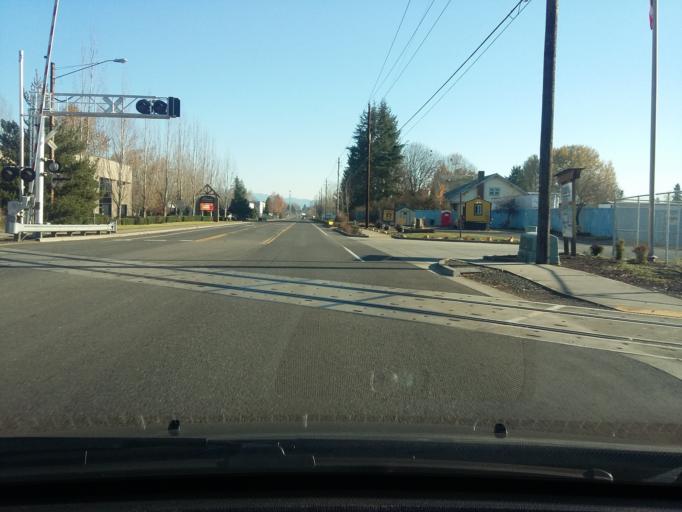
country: US
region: Washington
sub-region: Clark County
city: Barberton
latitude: 45.6860
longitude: -122.6159
